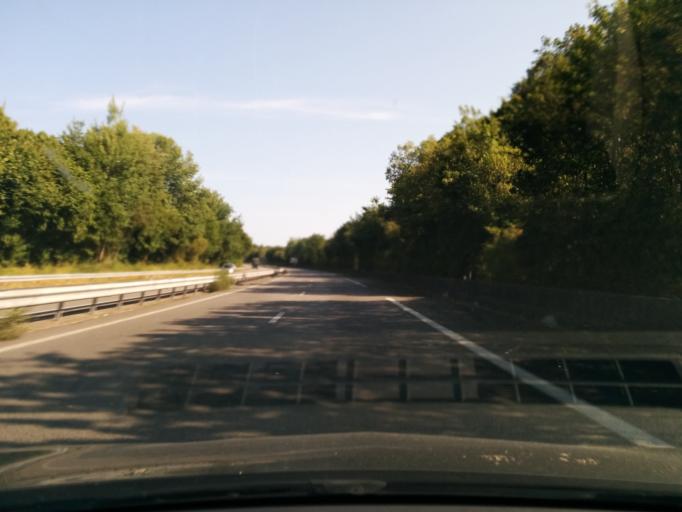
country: FR
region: Limousin
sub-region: Departement de la Haute-Vienne
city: Saint-Germain-les-Belles
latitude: 45.5988
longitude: 1.4484
